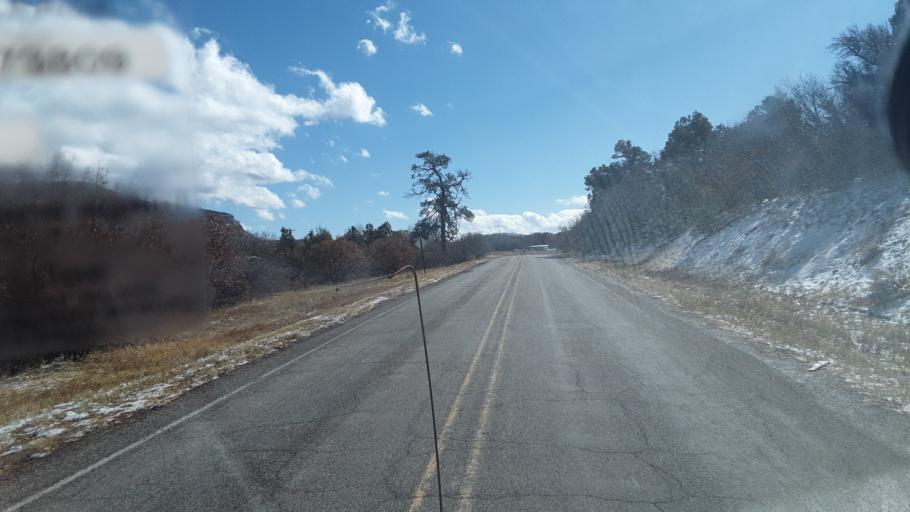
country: US
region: New Mexico
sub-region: Rio Arriba County
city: Santa Teresa
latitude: 36.2291
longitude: -106.8023
